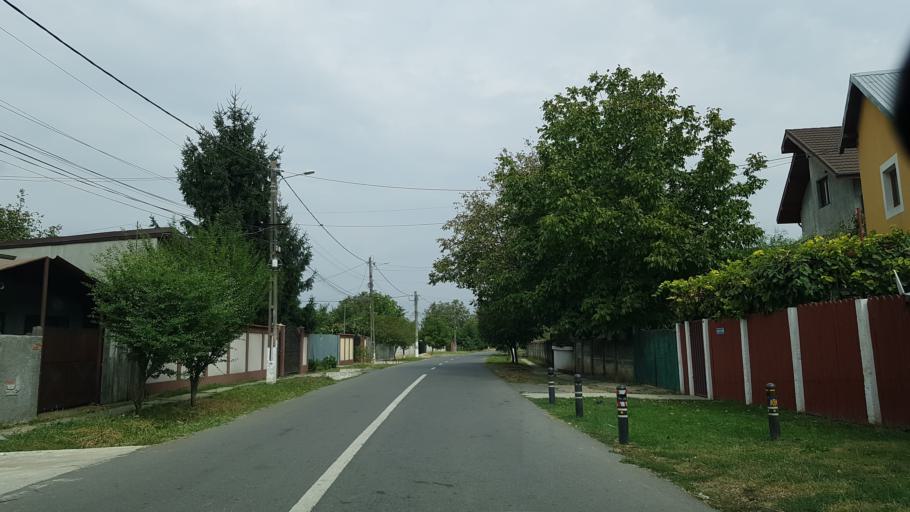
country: RO
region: Ilfov
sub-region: Comuna Ganeasa
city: Ganeasa
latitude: 44.4915
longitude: 26.2858
